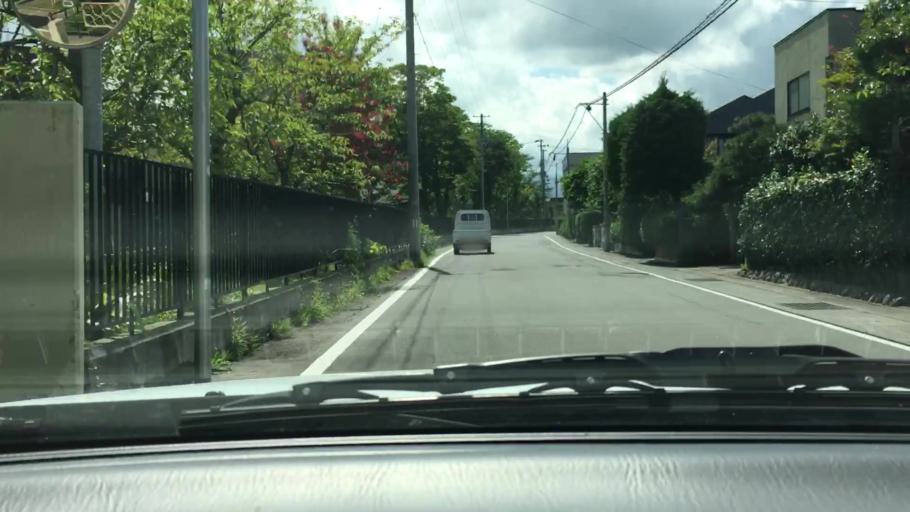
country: JP
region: Aomori
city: Hirosaki
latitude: 40.5894
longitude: 140.4707
